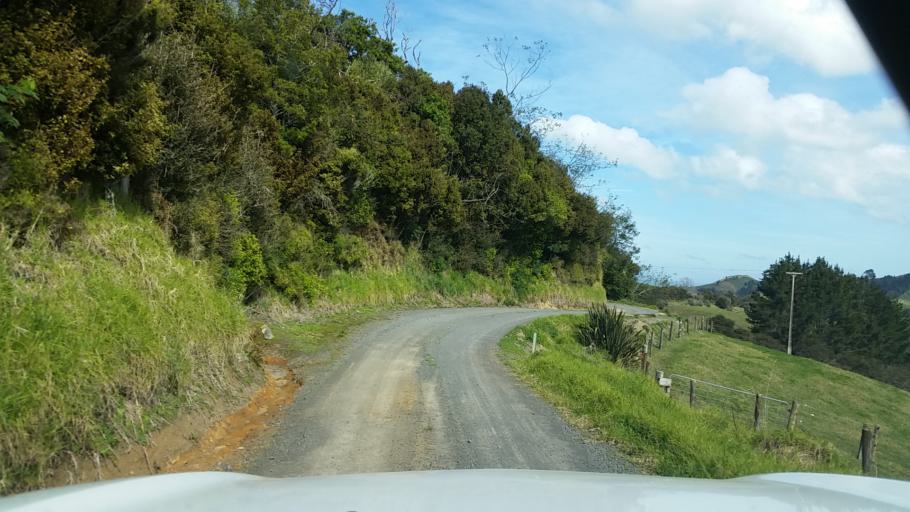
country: NZ
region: Waikato
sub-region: Hauraki District
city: Ngatea
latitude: -37.4601
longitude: 175.4696
